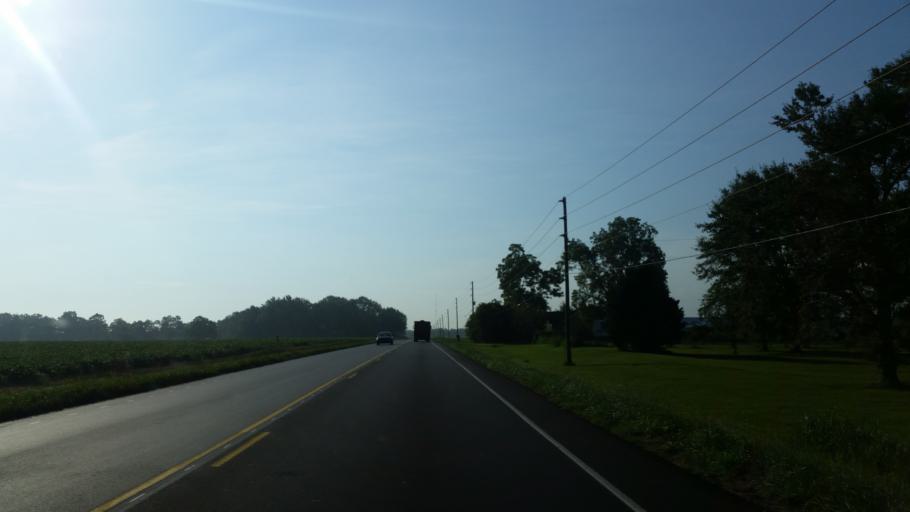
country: US
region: Alabama
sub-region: Baldwin County
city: Elberta
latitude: 30.5431
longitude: -87.5713
